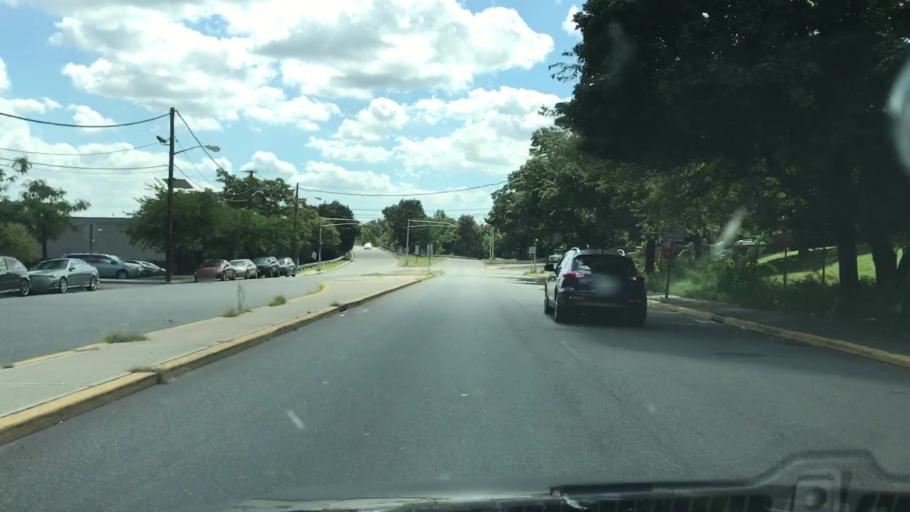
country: US
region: New Jersey
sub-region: Passaic County
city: Passaic
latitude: 40.8598
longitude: -74.1224
